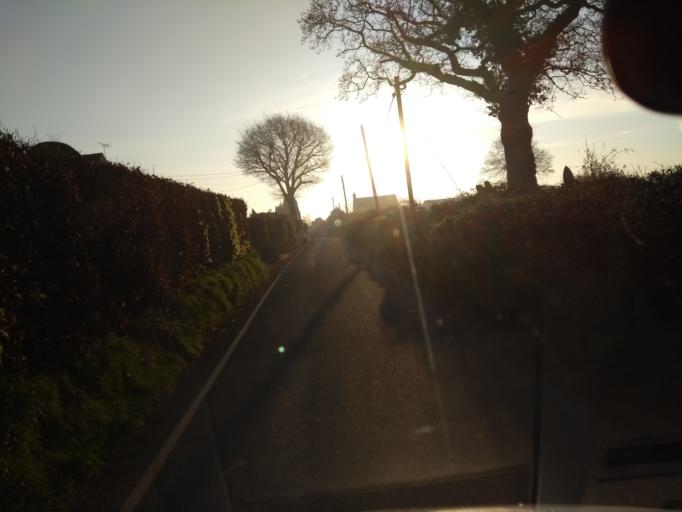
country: GB
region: England
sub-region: Somerset
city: Crewkerne
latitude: 50.8404
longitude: -2.8352
